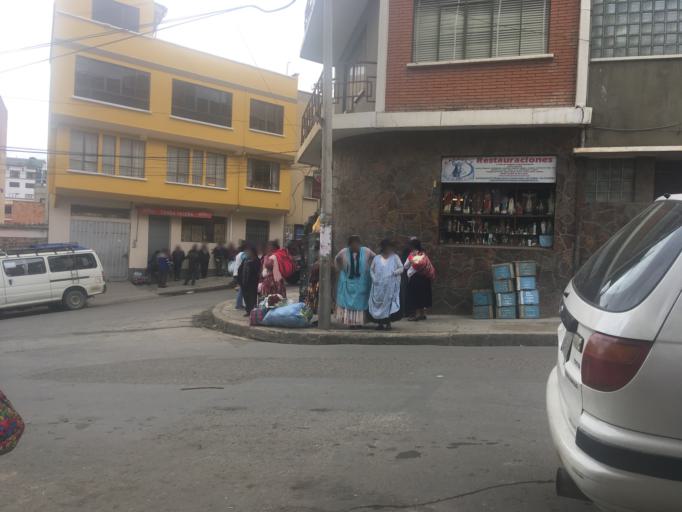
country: BO
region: La Paz
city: La Paz
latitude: -16.5019
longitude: -68.1399
